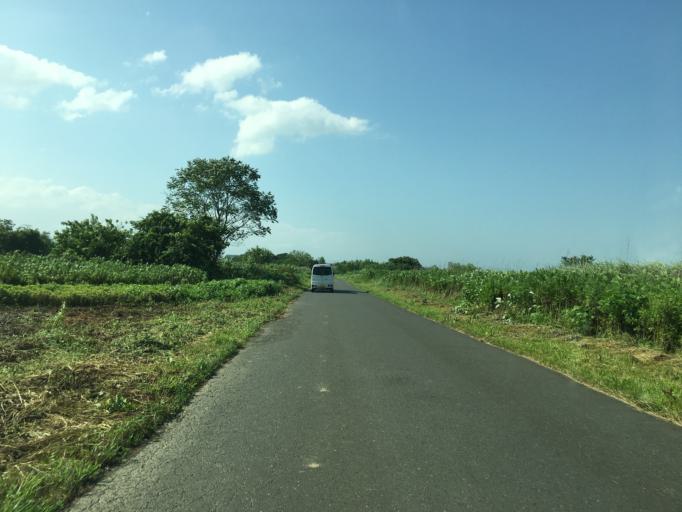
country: JP
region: Miyagi
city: Kakuda
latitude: 37.9625
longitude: 140.7898
